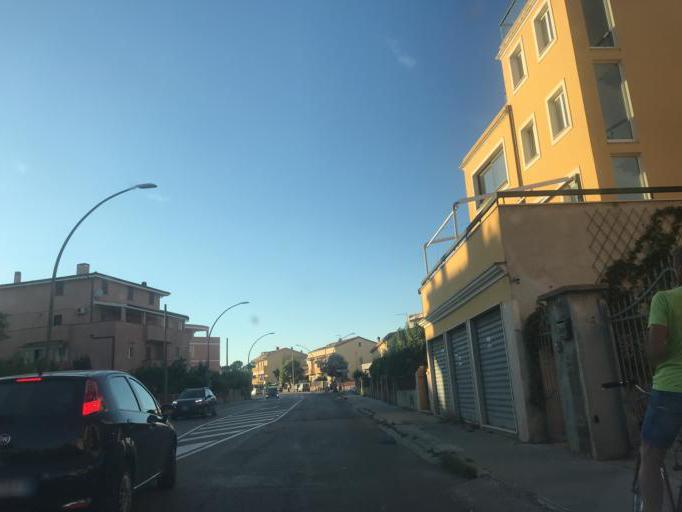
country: IT
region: Sardinia
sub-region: Provincia di Sassari
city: Alghero
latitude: 40.5821
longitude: 8.3181
